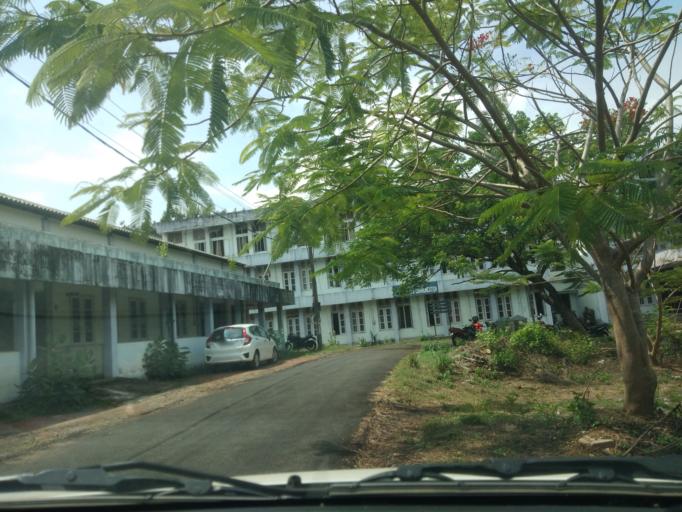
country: IN
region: Kerala
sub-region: Ernakulam
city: Elur
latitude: 10.0458
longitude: 76.3261
